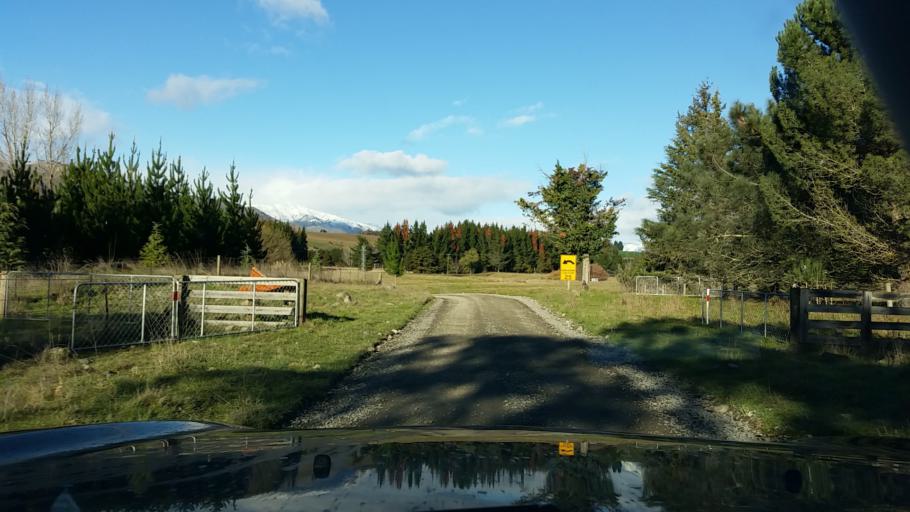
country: NZ
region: Marlborough
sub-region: Marlborough District
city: Blenheim
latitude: -41.6196
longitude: 173.6843
